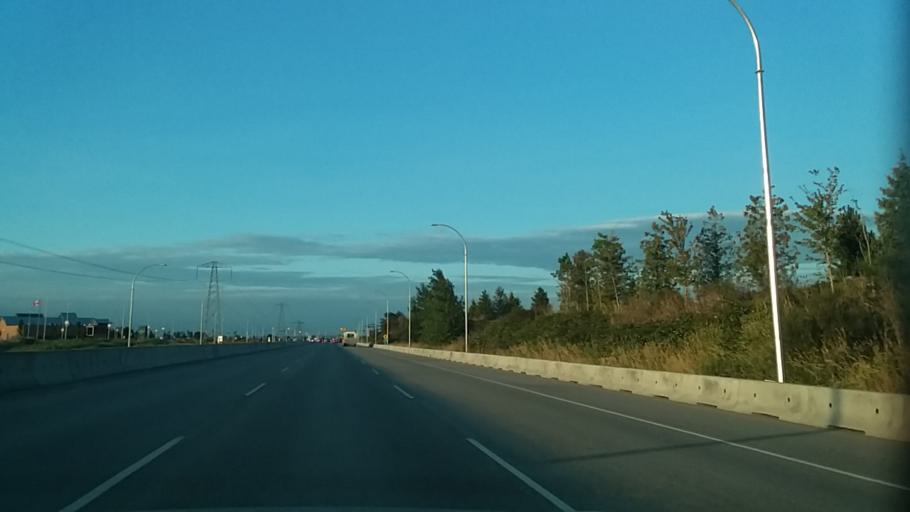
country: US
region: Washington
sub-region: Whatcom County
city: Point Roberts
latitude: 49.0346
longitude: -123.0856
